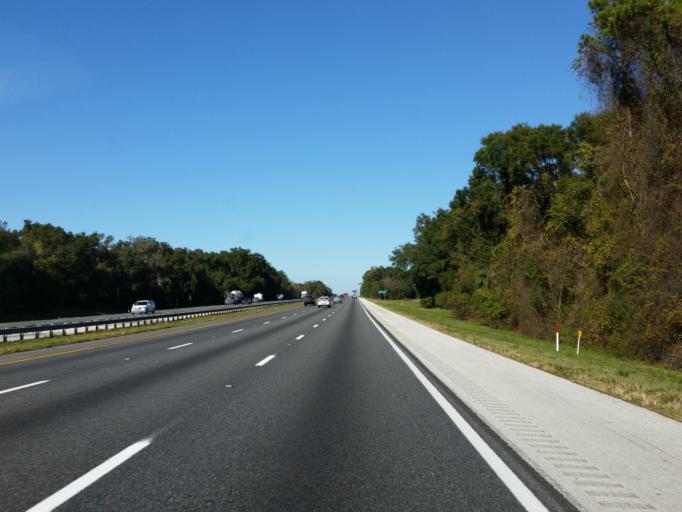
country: US
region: Florida
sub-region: Marion County
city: Ocala
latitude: 29.1072
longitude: -82.1848
